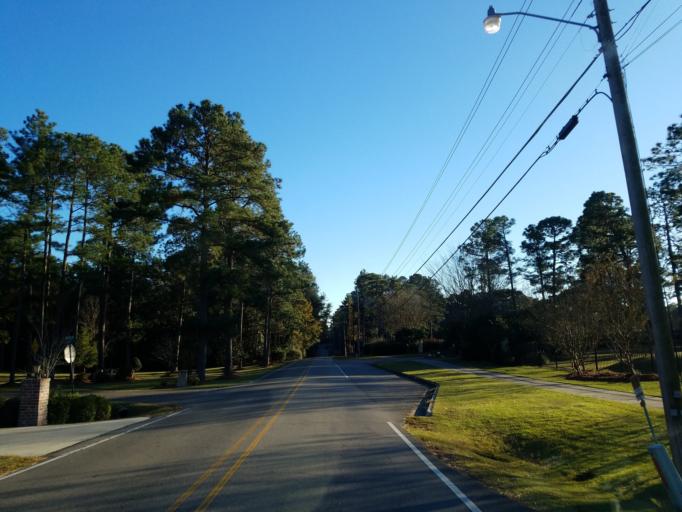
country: US
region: Mississippi
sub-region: Lamar County
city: Arnold Line
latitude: 31.3519
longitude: -89.3776
